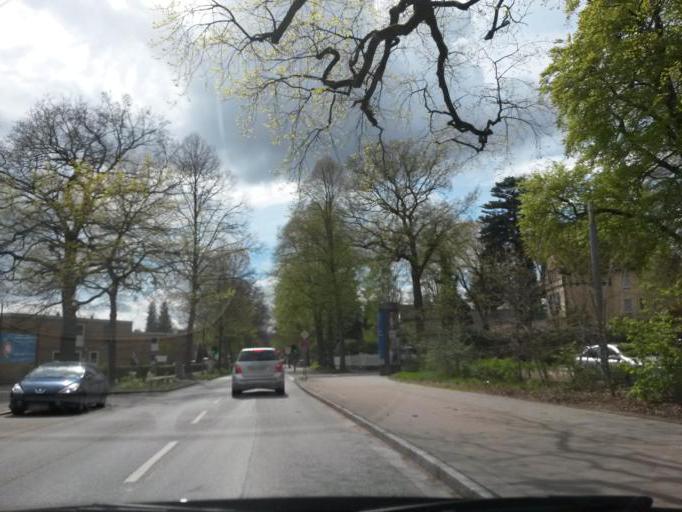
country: DE
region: Hamburg
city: Winterhude
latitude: 53.6162
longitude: 9.9870
